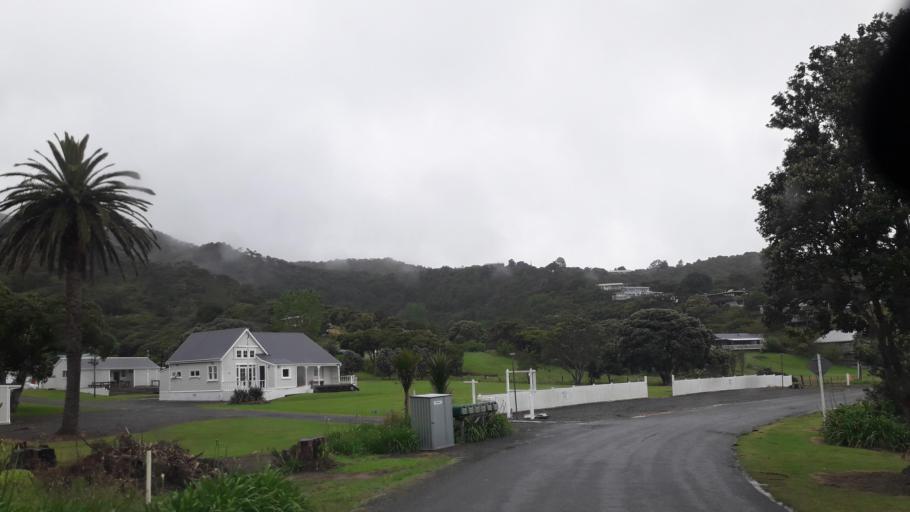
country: NZ
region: Northland
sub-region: Far North District
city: Paihia
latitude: -35.2355
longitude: 174.2606
